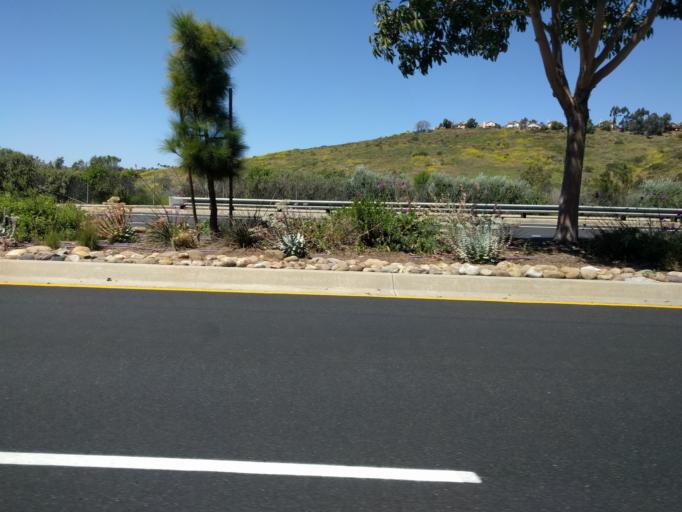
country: US
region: California
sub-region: San Diego County
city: Fairbanks Ranch
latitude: 32.9400
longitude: -117.1235
